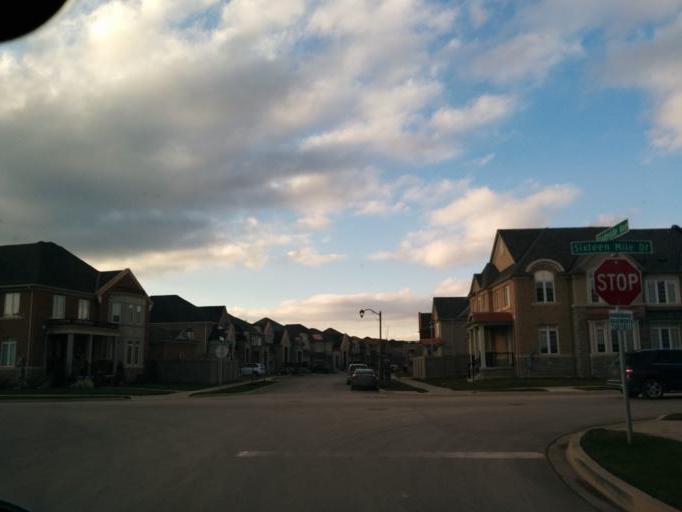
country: CA
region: Ontario
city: Oakville
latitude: 43.4678
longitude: -79.7456
